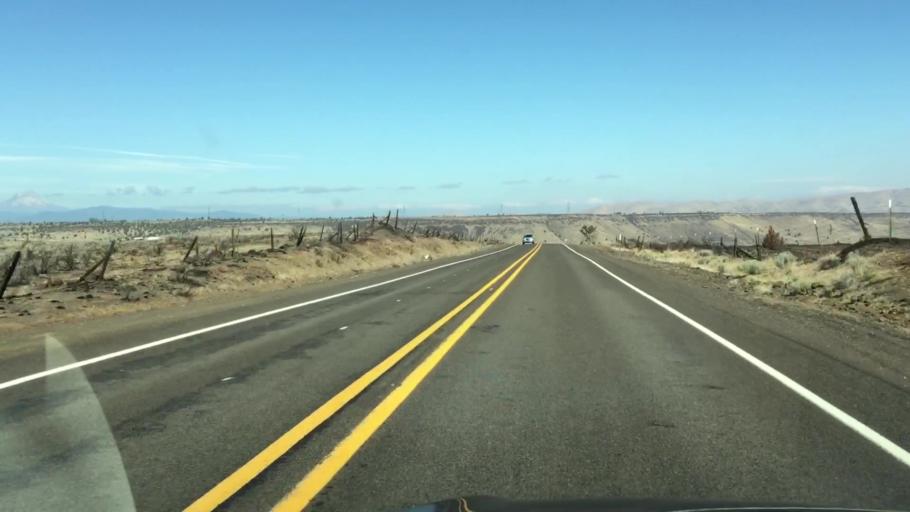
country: US
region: Oregon
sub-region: Jefferson County
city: Warm Springs
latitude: 45.1554
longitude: -121.0664
